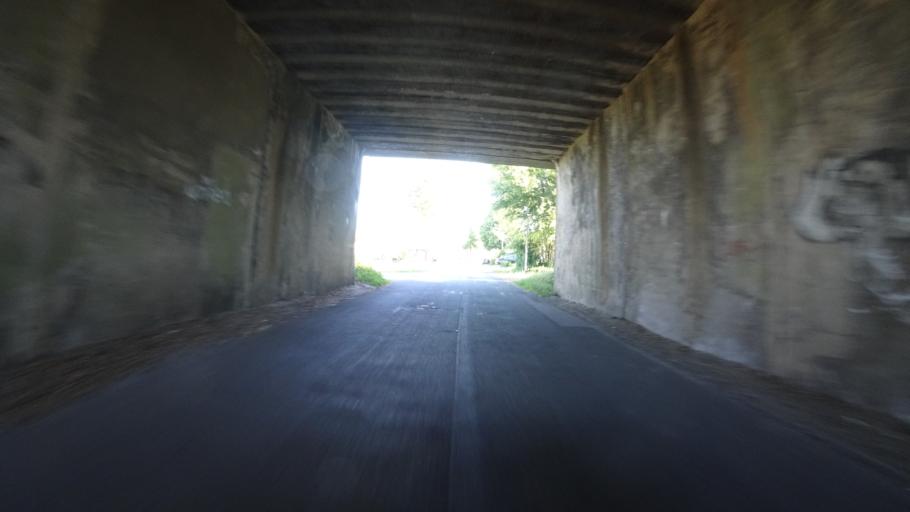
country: DE
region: North Rhine-Westphalia
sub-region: Regierungsbezirk Detmold
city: Rheda-Wiedenbruck
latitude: 51.8608
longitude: 8.3065
